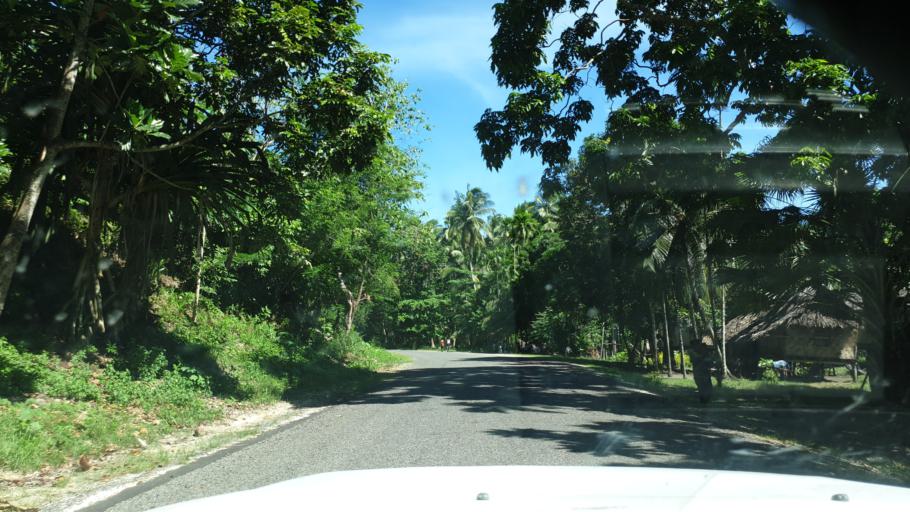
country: PG
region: Madang
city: Madang
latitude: -4.5227
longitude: 145.4698
